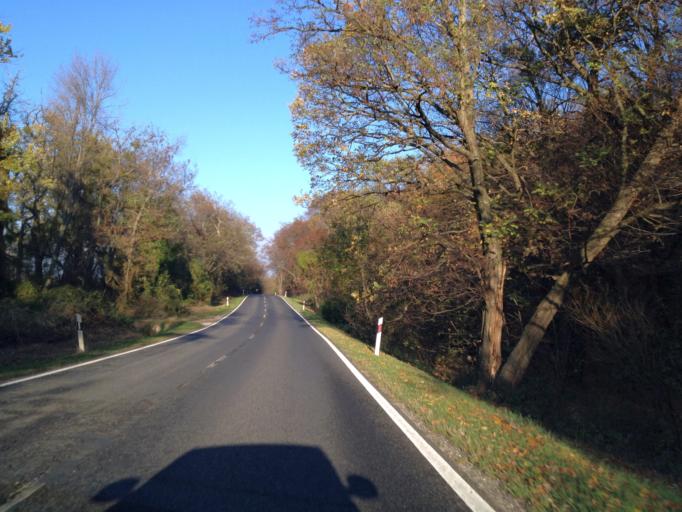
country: HU
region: Veszprem
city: Zirc
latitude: 47.3311
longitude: 17.8813
